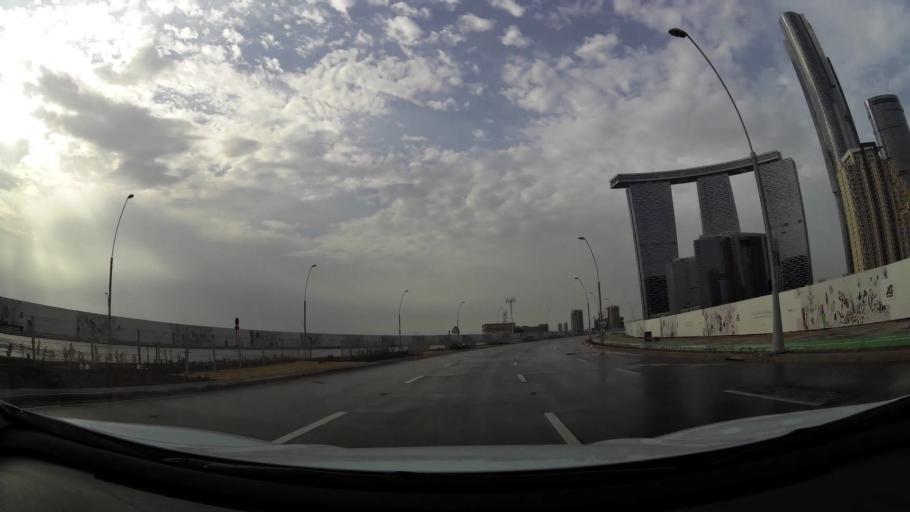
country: AE
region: Abu Dhabi
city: Abu Dhabi
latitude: 24.4980
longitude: 54.4126
